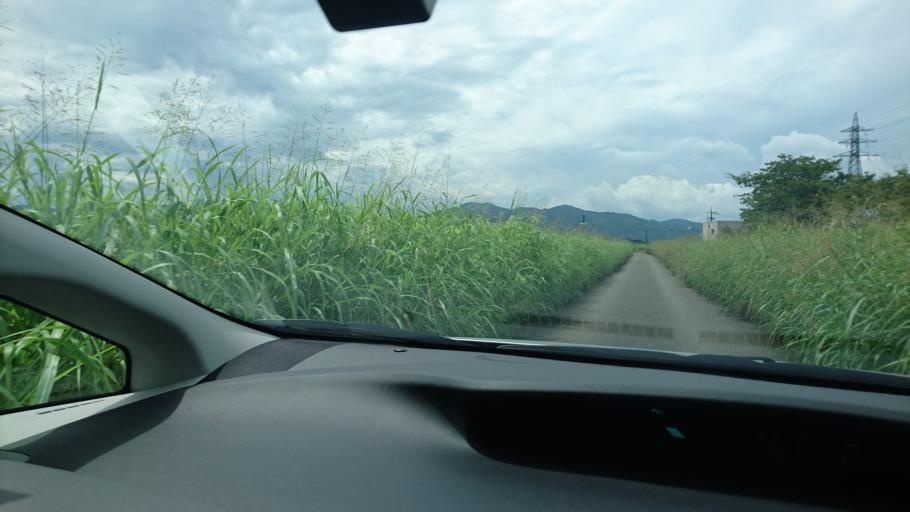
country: JP
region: Saga Prefecture
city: Takeocho-takeo
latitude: 33.2110
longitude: 130.1097
